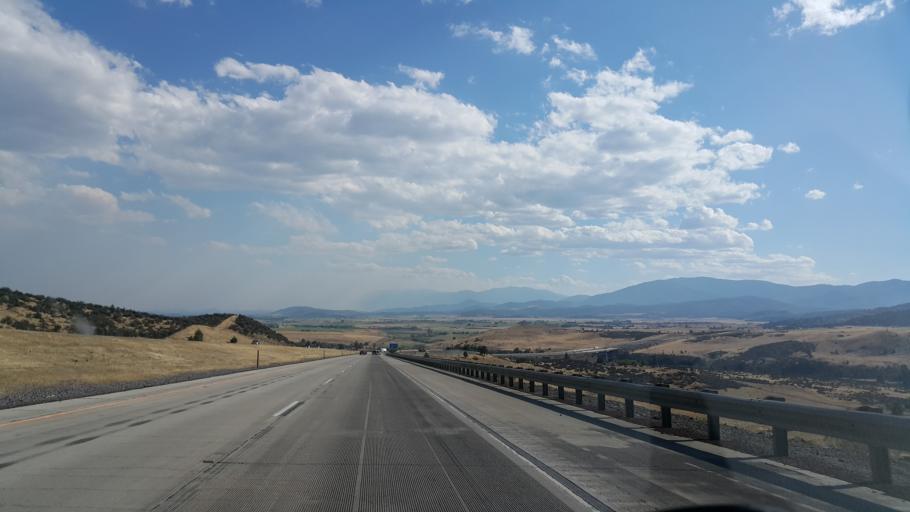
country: US
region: California
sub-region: Siskiyou County
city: Yreka
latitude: 41.7825
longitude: -122.5843
